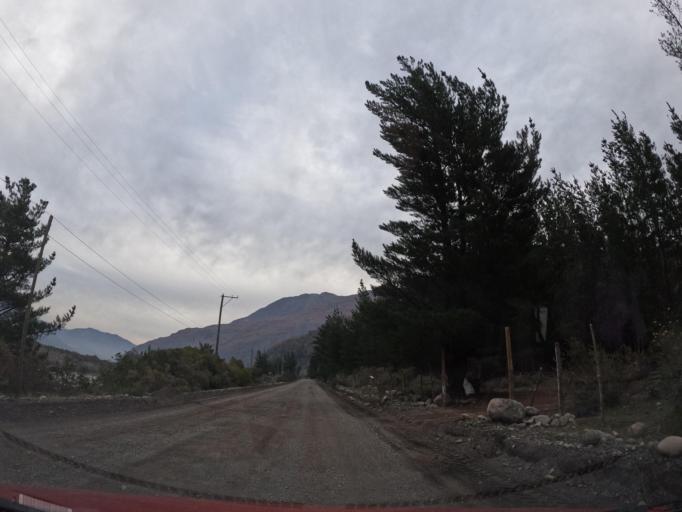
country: CL
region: Maule
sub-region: Provincia de Linares
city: Colbun
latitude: -35.7040
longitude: -71.0950
